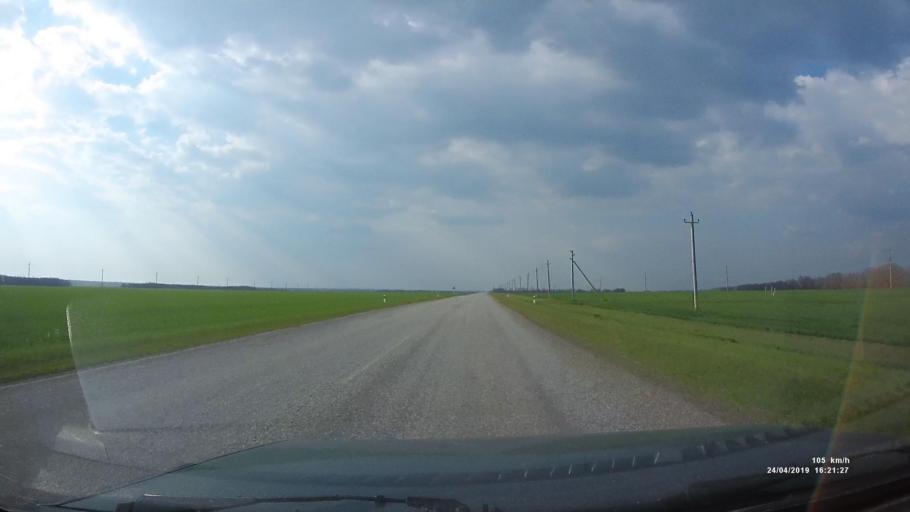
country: RU
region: Rostov
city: Orlovskiy
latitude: 46.8050
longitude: 42.0652
